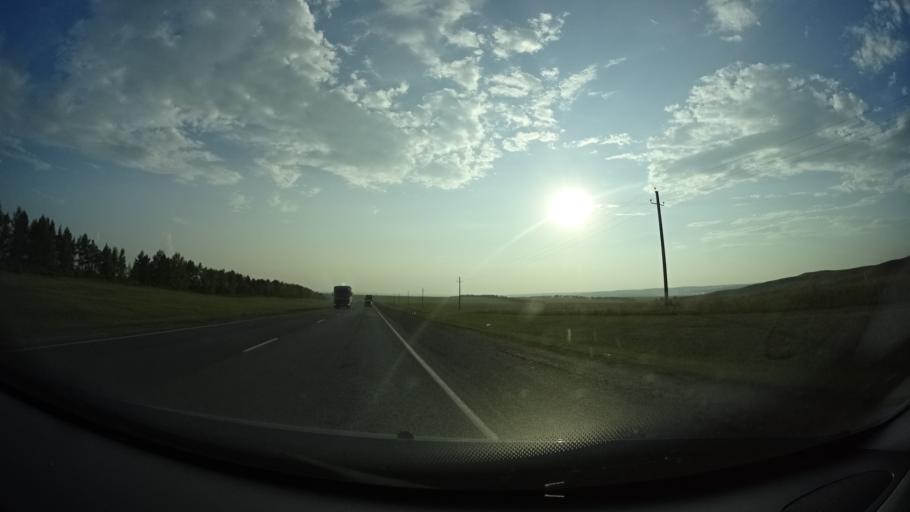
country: RU
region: Samara
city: Kamyshla
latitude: 54.0614
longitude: 52.1093
